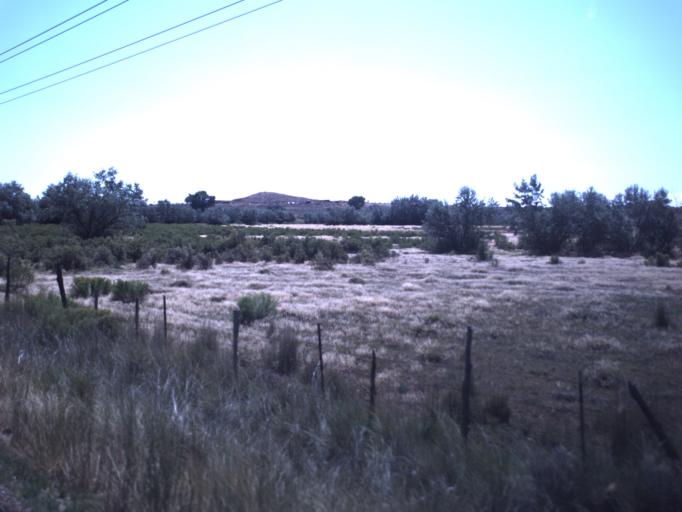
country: US
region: Utah
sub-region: Duchesne County
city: Roosevelt
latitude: 40.4037
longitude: -109.8360
